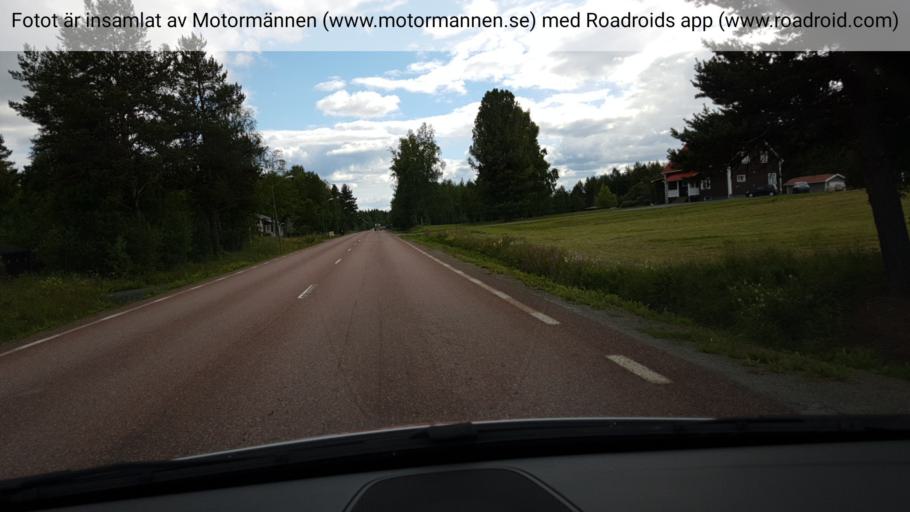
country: SE
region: Jaemtland
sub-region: Stroemsunds Kommun
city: Stroemsund
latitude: 63.9646
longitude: 15.8518
